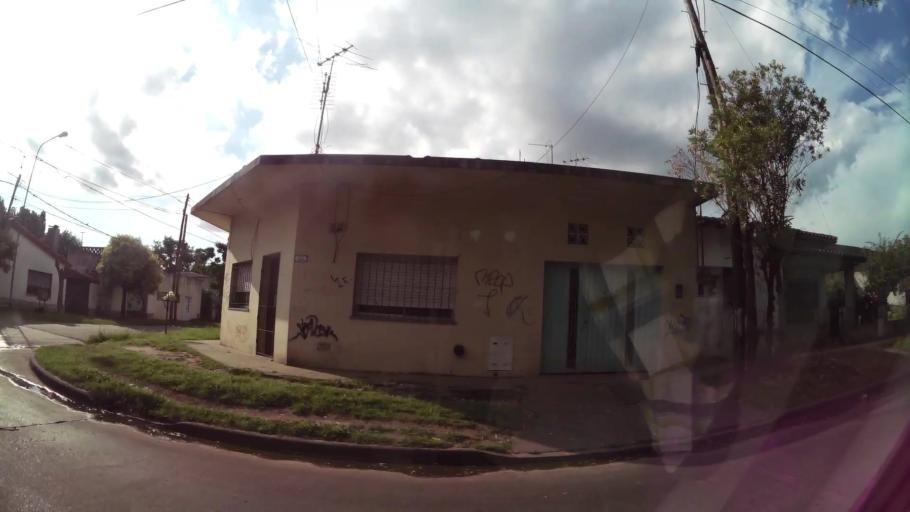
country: AR
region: Buenos Aires
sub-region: Partido de Tigre
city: Tigre
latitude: -34.4702
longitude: -58.6584
